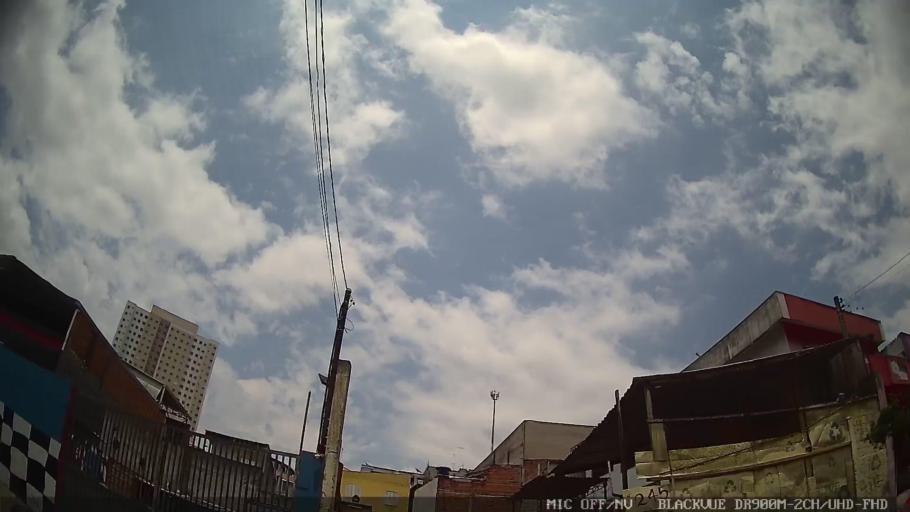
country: BR
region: Sao Paulo
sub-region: Caieiras
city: Caieiras
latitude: -23.4047
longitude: -46.7376
